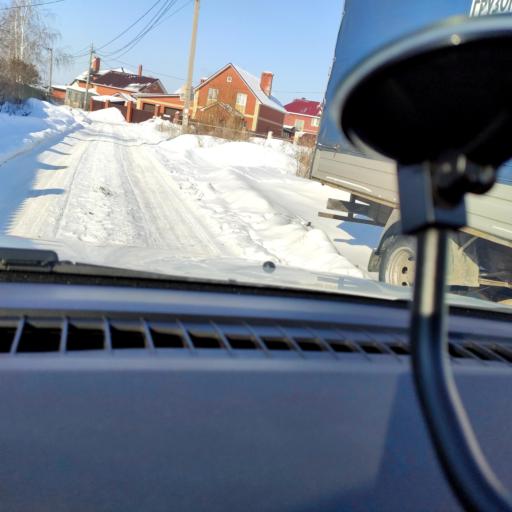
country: RU
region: Samara
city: Samara
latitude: 53.1375
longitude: 50.2492
